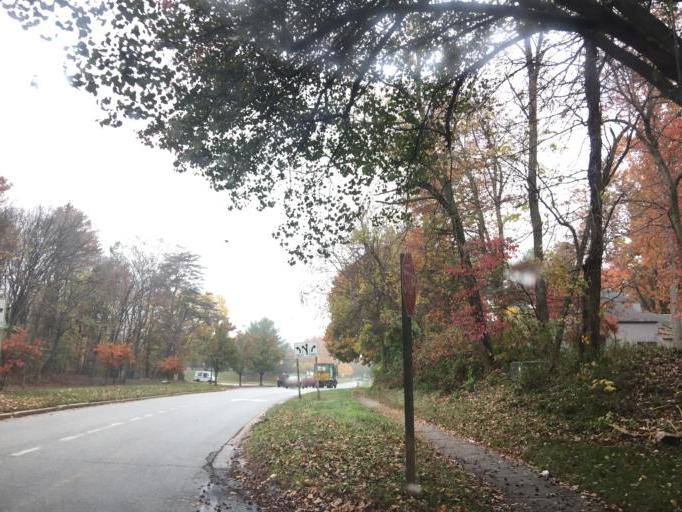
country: US
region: Maryland
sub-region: Howard County
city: Riverside
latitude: 39.1981
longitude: -76.8501
